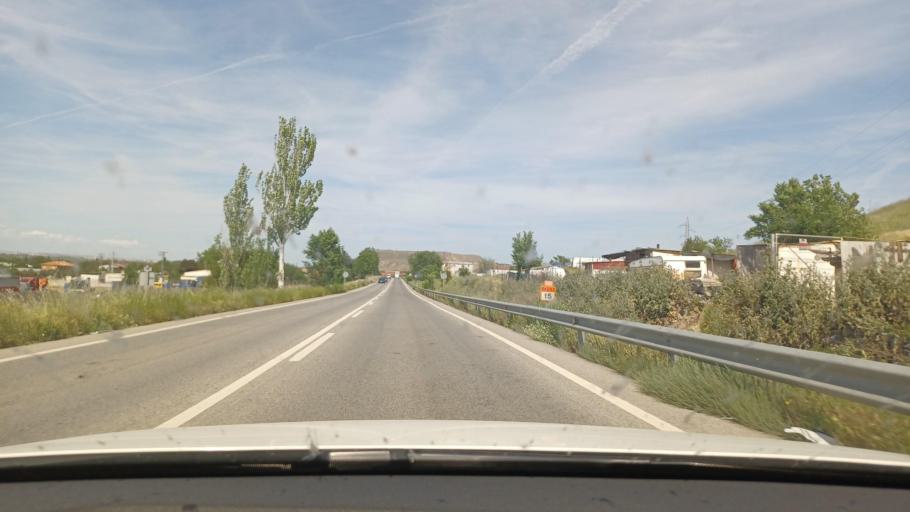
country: ES
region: Madrid
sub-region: Provincia de Madrid
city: Torrejon de Ardoz
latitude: 40.4244
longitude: -3.4551
